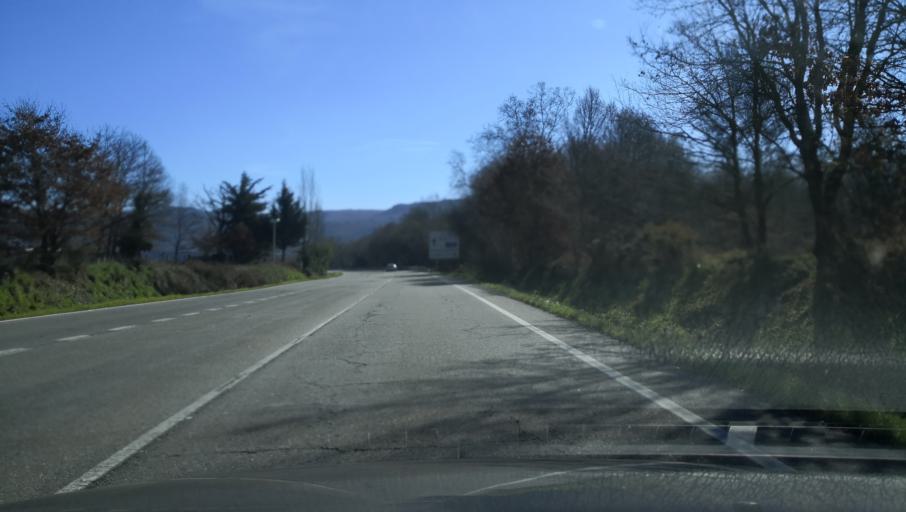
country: ES
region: Galicia
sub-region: Provincia de Ourense
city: Allariz
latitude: 42.2051
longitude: -7.8139
